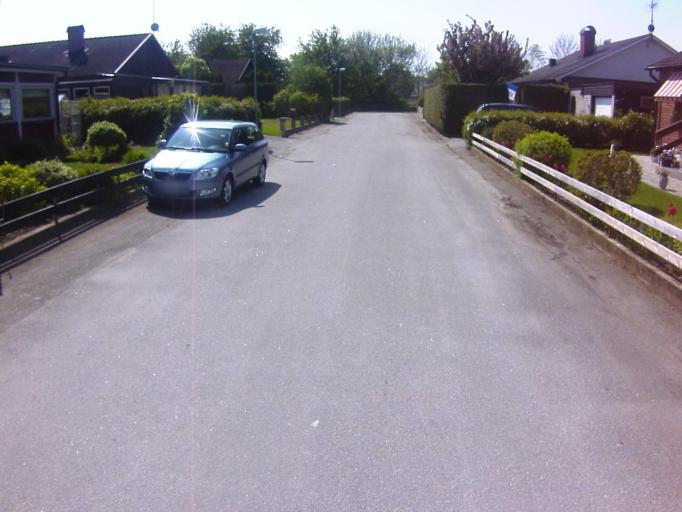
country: SE
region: Blekinge
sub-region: Solvesborgs Kommun
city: Soelvesborg
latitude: 56.0459
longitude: 14.6892
